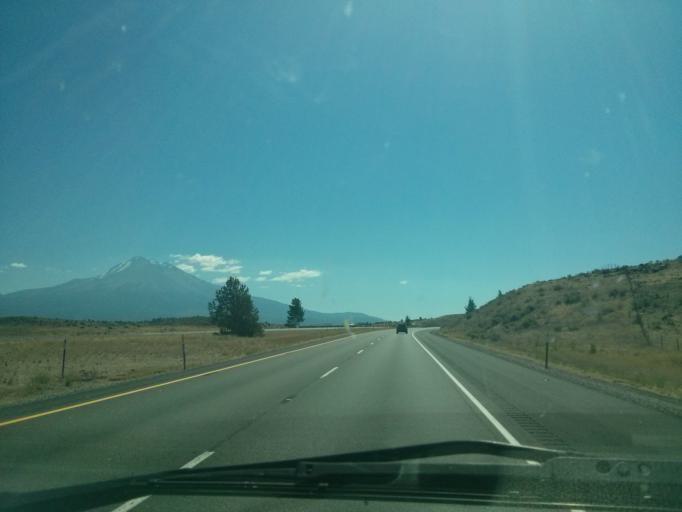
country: US
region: California
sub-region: Siskiyou County
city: Weed
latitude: 41.5001
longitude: -122.4672
